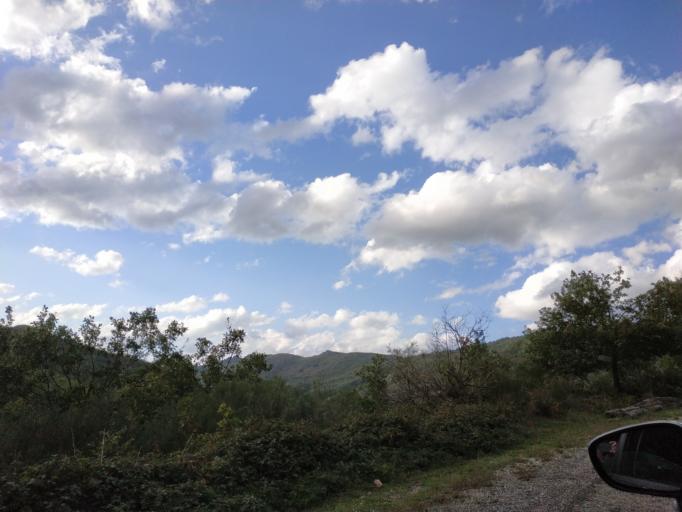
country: ES
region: Castille and Leon
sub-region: Provincia de Leon
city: Candin
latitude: 42.8611
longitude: -6.8538
